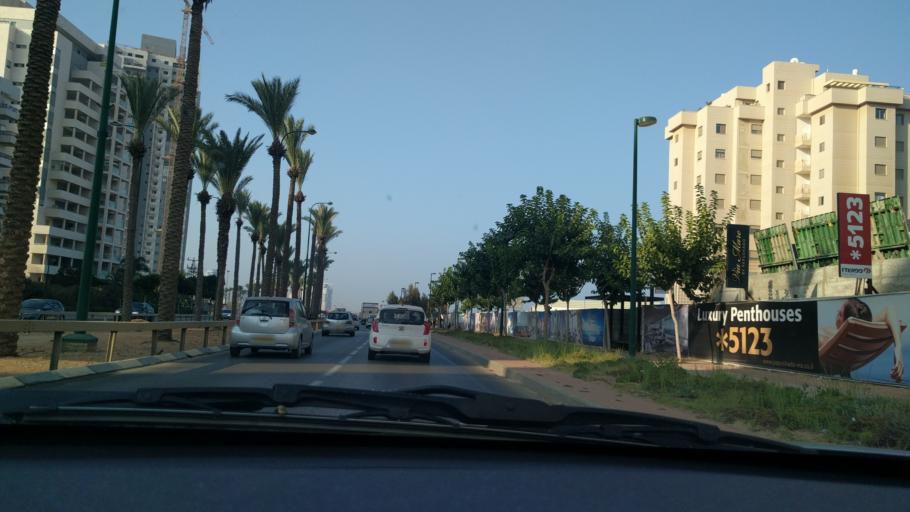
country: IL
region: Central District
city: Netanya
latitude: 32.2954
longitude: 34.8430
